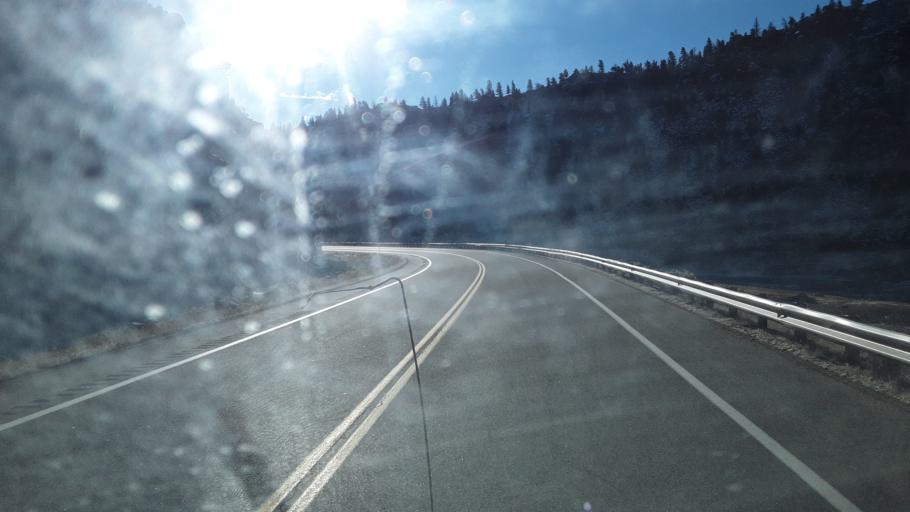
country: US
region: Colorado
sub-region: Gunnison County
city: Gunnison
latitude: 38.4876
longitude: -107.0533
